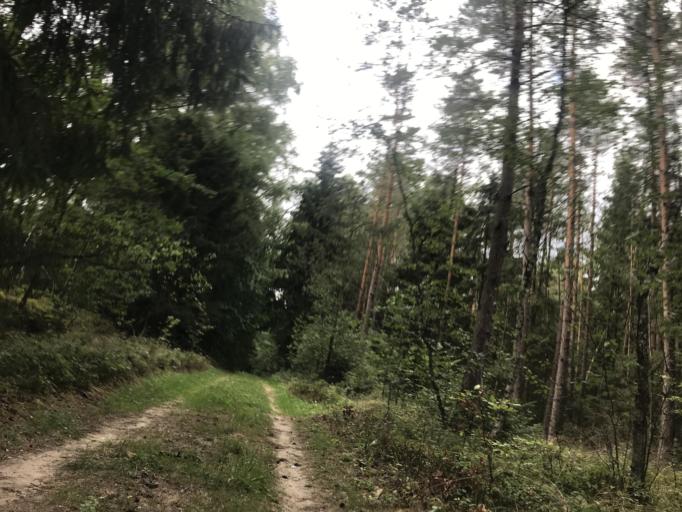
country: DE
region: Lower Saxony
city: Barendorf
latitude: 53.2365
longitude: 10.5378
